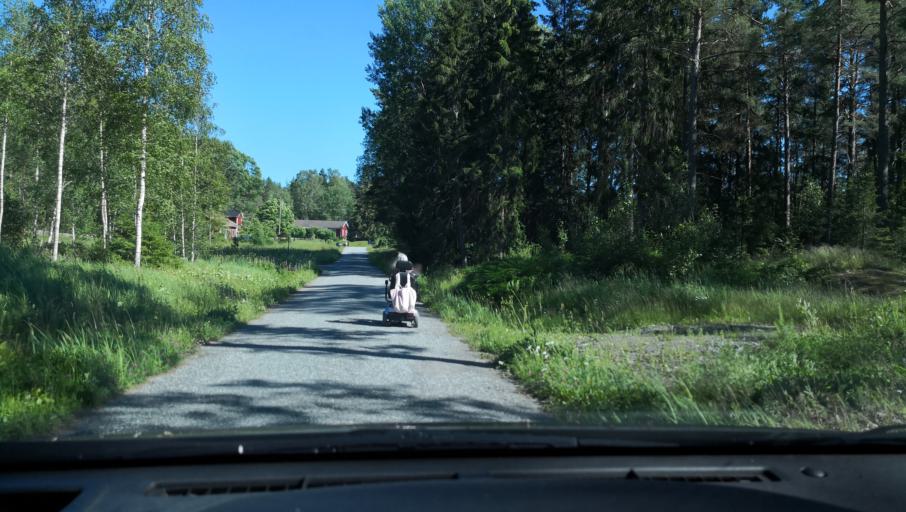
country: SE
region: Soedermanland
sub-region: Eskilstuna Kommun
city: Eskilstuna
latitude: 59.3431
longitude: 16.5597
